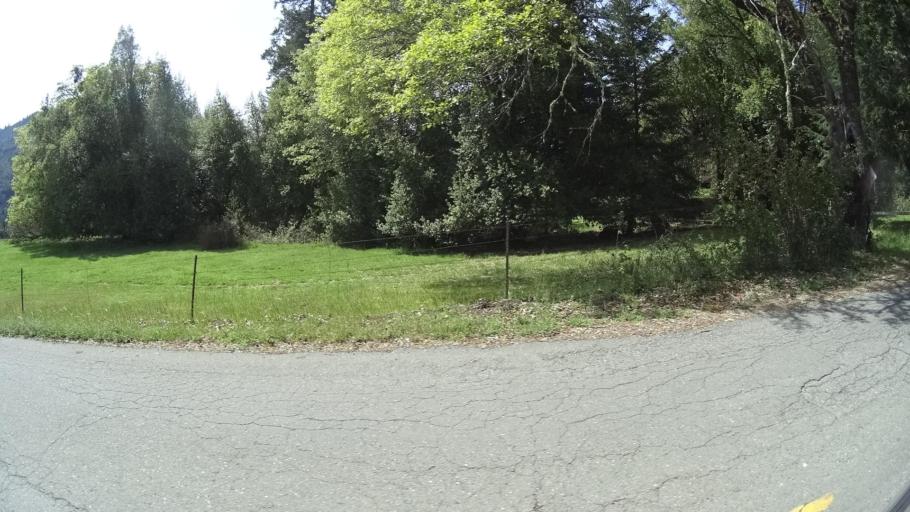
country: US
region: California
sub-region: Humboldt County
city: Redway
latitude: 40.3929
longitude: -123.7471
